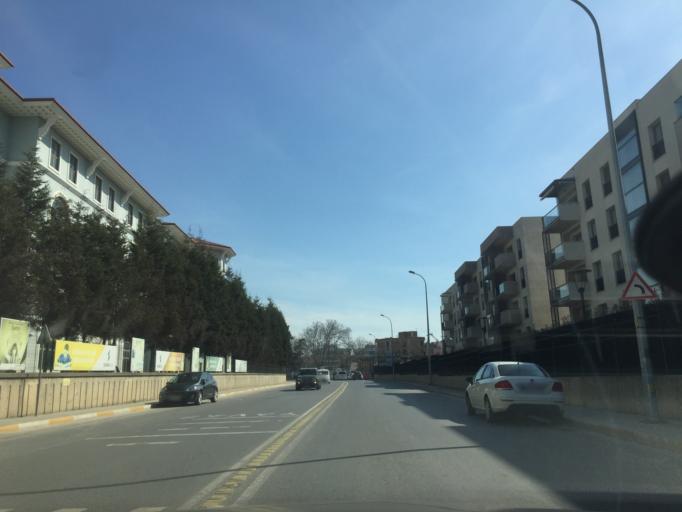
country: TR
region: Istanbul
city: Icmeler
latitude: 40.8317
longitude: 29.3176
